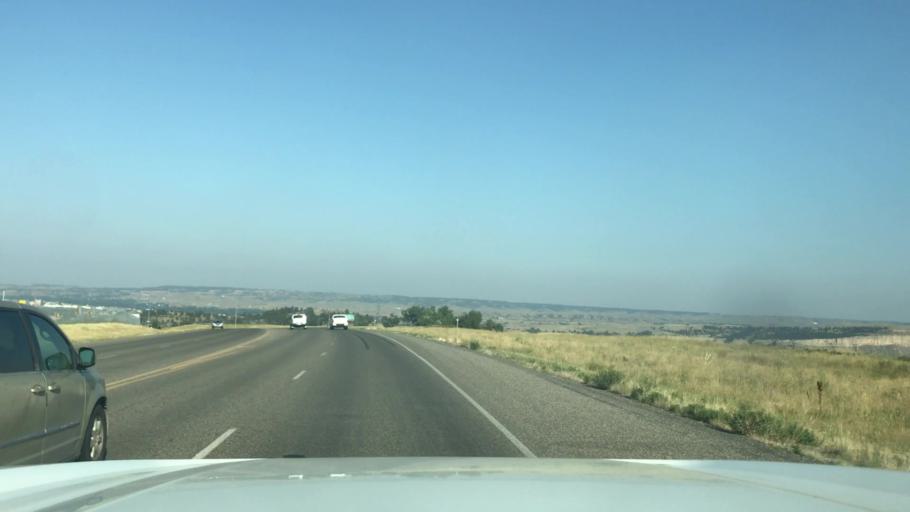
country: US
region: Montana
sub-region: Yellowstone County
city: Billings
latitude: 45.7995
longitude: -108.5118
